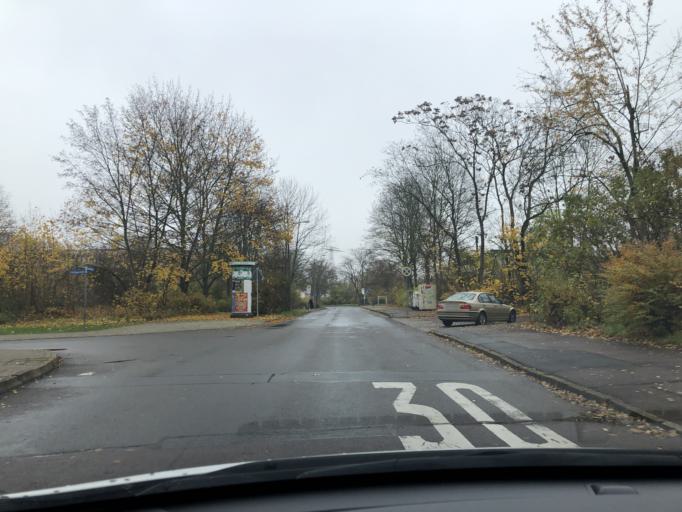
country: DE
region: Saxony-Anhalt
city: Halle Neustadt
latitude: 51.4763
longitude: 11.9394
